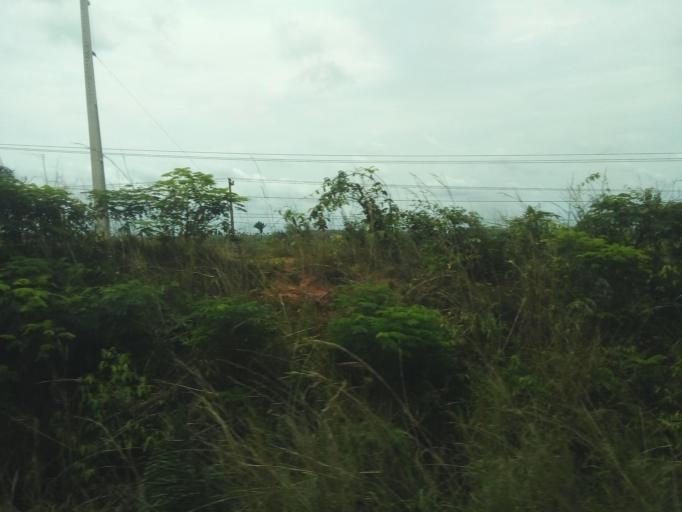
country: BR
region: Maranhao
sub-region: Santa Ines
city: Santa Ines
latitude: -3.6730
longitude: -45.8665
